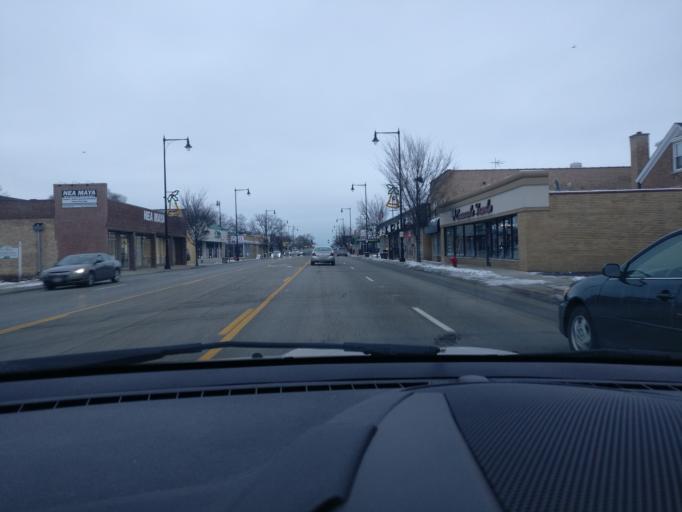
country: US
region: Illinois
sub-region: Cook County
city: Morton Grove
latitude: 42.0409
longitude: -87.7702
